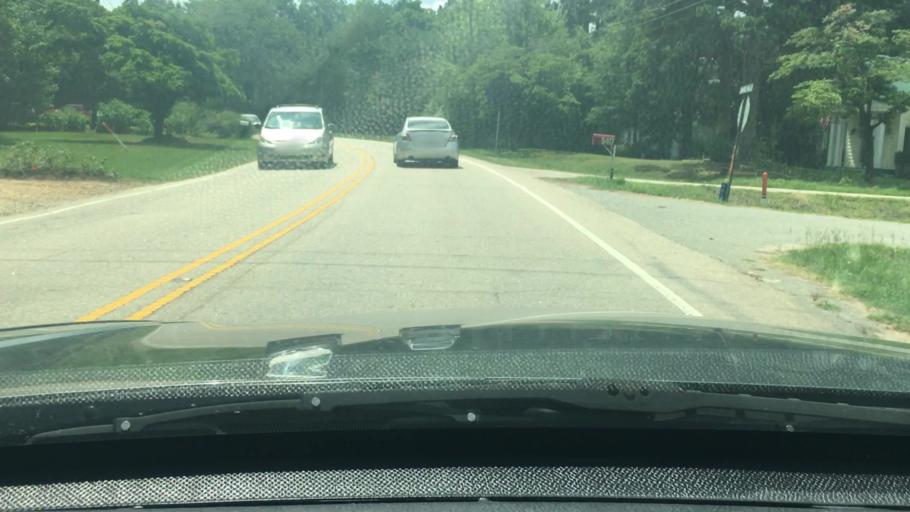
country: US
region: North Carolina
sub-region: Wake County
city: Cary
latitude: 35.8012
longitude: -78.8039
